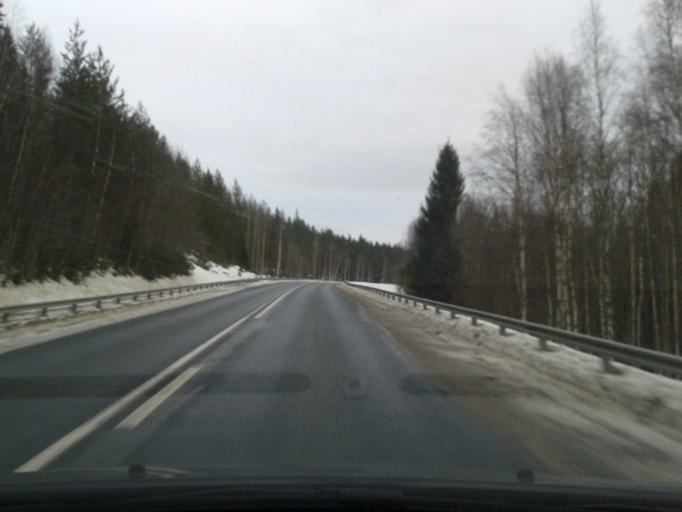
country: SE
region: Vaesternorrland
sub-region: Solleftea Kommun
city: Solleftea
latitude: 63.4088
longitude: 16.9702
